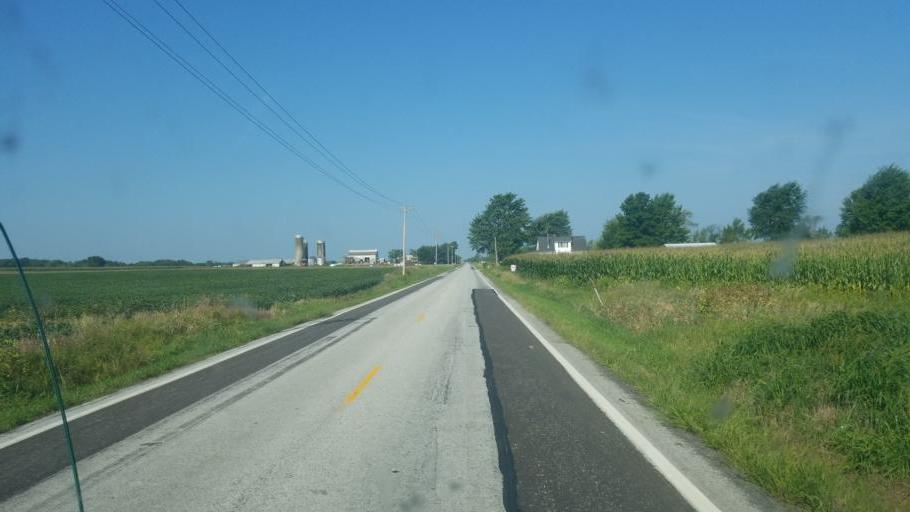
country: US
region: Ohio
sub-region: Lorain County
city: Wellington
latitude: 41.1002
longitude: -82.1345
